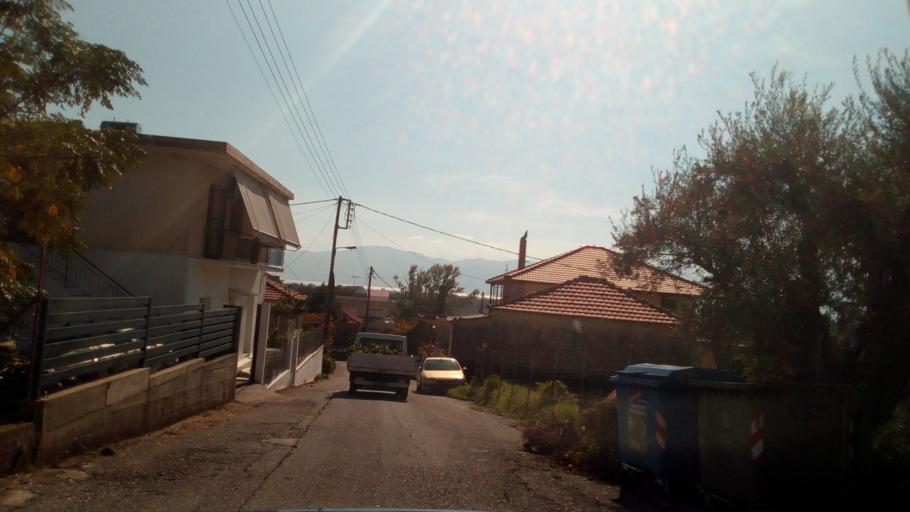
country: GR
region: West Greece
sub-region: Nomos Aitolias kai Akarnanias
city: Nafpaktos
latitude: 38.4155
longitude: 21.8744
